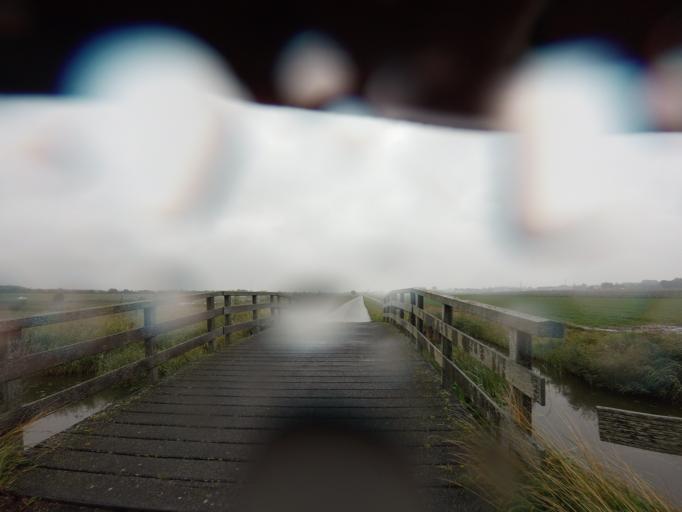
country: NL
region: North Holland
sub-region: Gemeente Medemblik
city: Opperdoes
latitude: 52.7666
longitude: 5.0749
